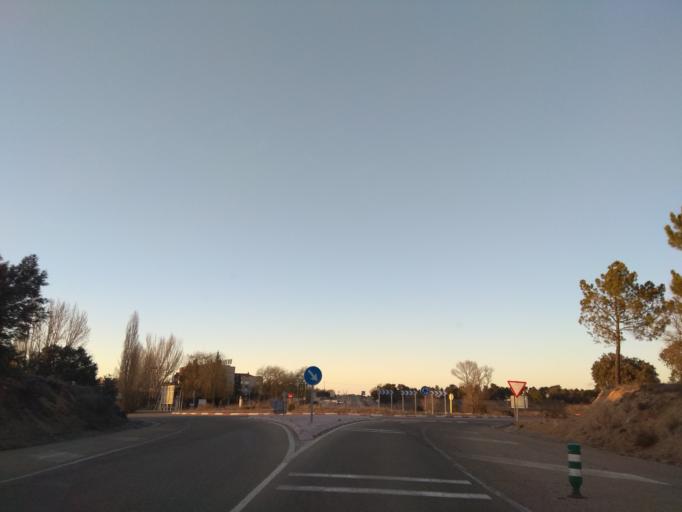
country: ES
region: Castille and Leon
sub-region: Provincia de Burgos
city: Aranda de Duero
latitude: 41.7085
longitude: -3.6870
